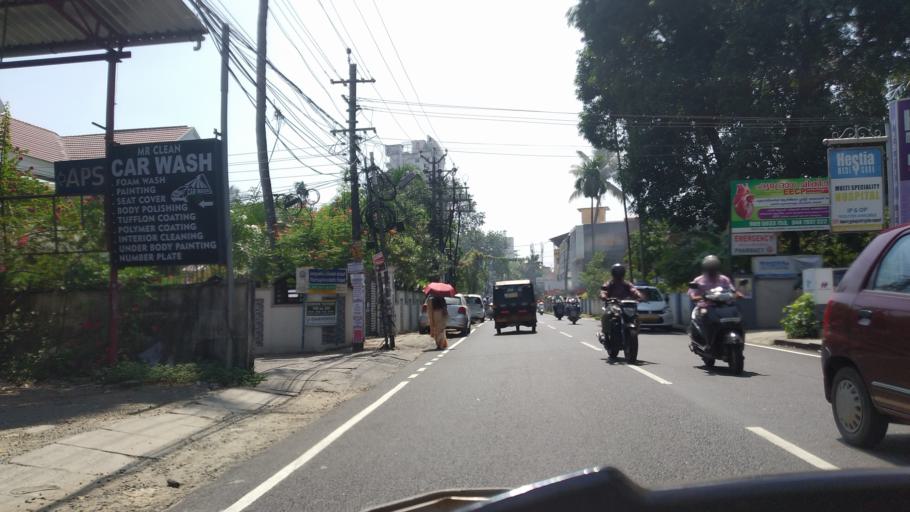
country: IN
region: Kerala
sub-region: Ernakulam
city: Elur
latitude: 10.0003
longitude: 76.3069
